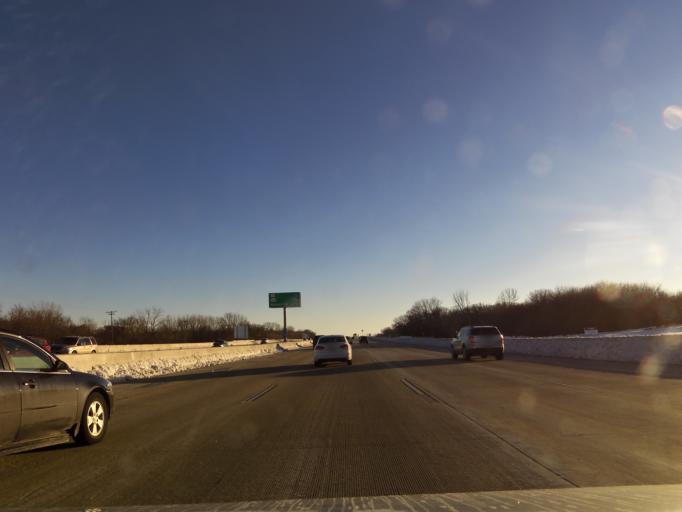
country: US
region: Wisconsin
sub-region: Kenosha County
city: Pleasant Prairie
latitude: 42.5566
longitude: -87.9527
